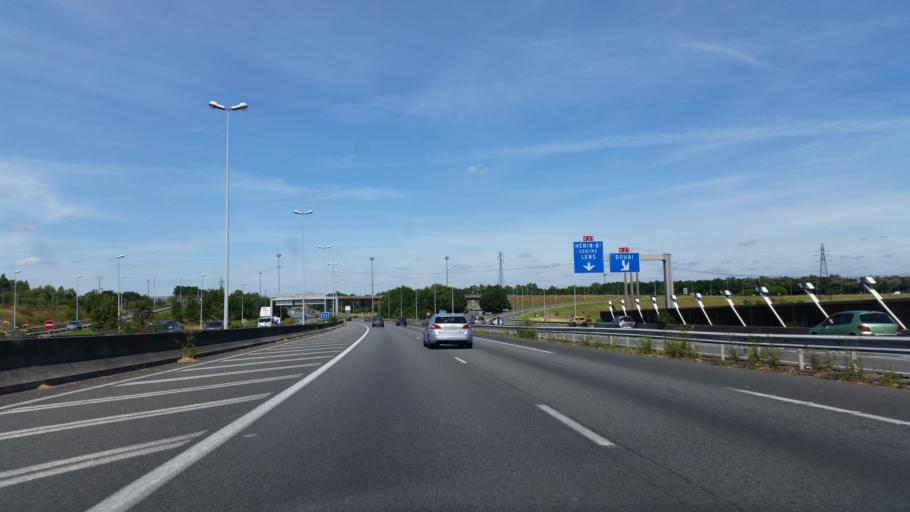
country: FR
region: Nord-Pas-de-Calais
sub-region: Departement du Pas-de-Calais
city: Noyelles-Godault
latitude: 50.4214
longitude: 2.9851
